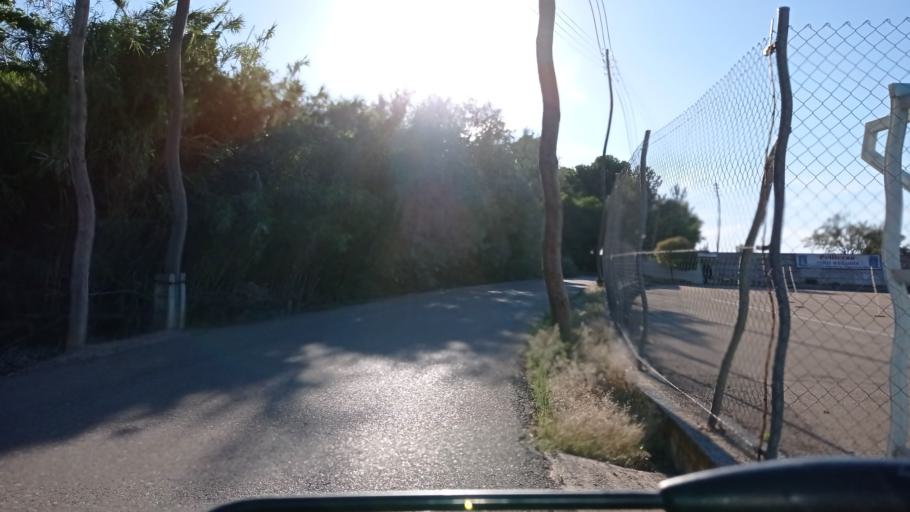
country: ES
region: Aragon
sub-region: Provincia de Zaragoza
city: Oliver-Valdefierro, Oliver, Valdefierro
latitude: 41.6637
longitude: -0.9520
